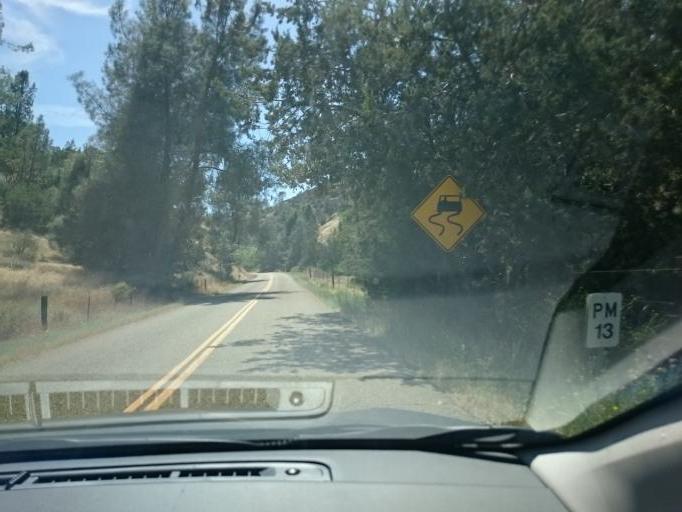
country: US
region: California
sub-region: Stanislaus County
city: Patterson
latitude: 37.4289
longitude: -121.3374
